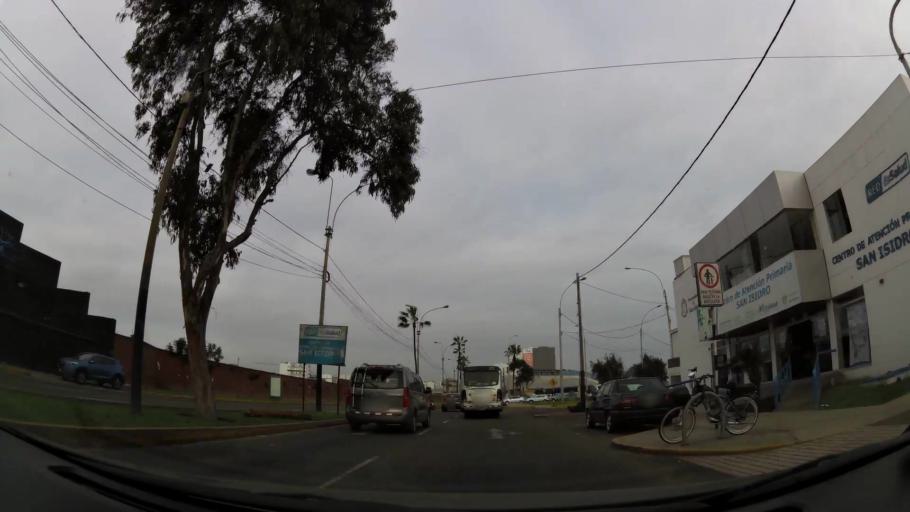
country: PE
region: Lima
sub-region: Lima
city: San Isidro
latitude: -12.1083
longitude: -77.0534
